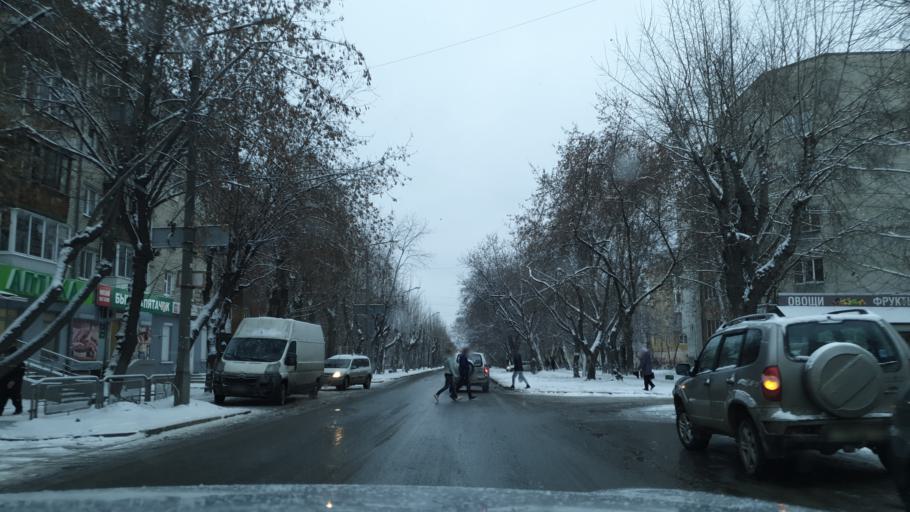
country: RU
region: Sverdlovsk
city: Istok
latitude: 56.7527
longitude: 60.7087
